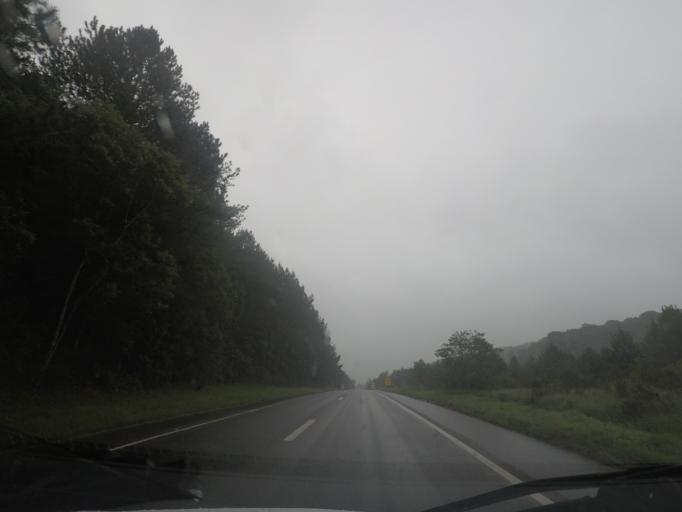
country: BR
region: Sao Paulo
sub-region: Cajati
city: Cajati
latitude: -24.9678
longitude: -48.4402
